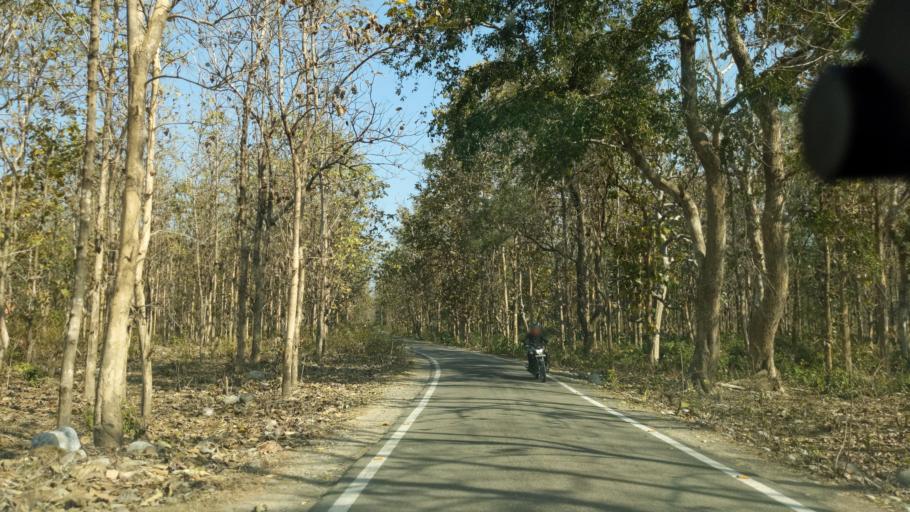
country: IN
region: Uttarakhand
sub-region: Naini Tal
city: Ramnagar
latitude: 29.4246
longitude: 79.1393
